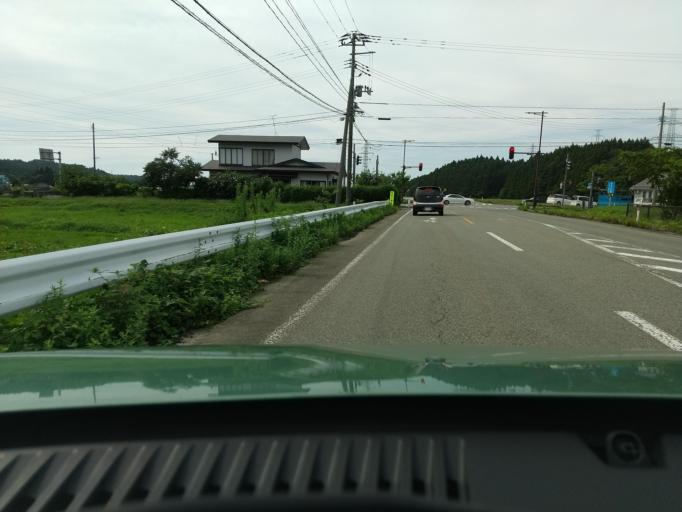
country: JP
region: Akita
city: Akita Shi
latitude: 39.7909
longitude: 140.1121
